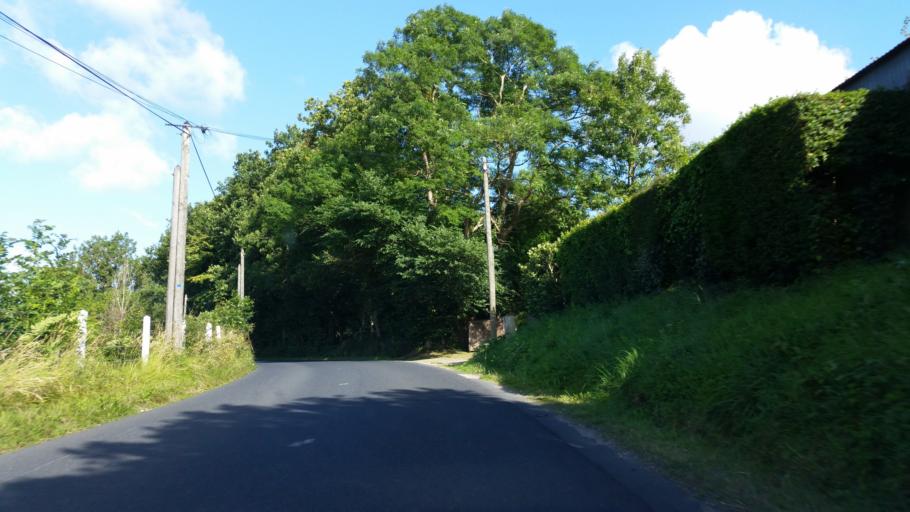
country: FR
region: Lower Normandy
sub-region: Departement du Calvados
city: Touques
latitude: 49.3379
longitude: 0.1291
